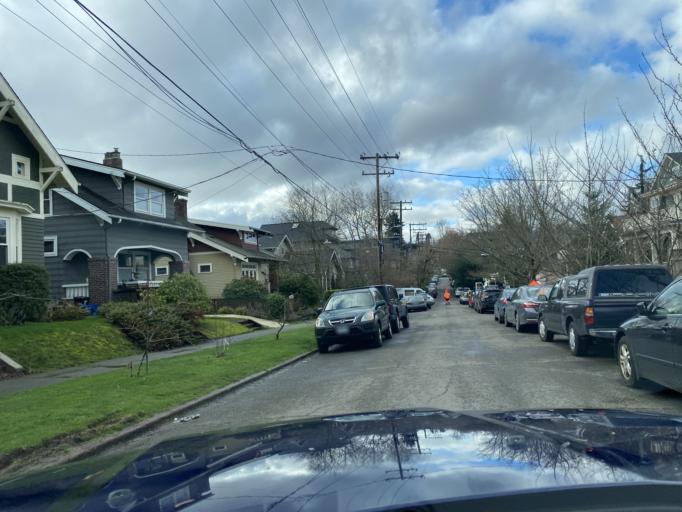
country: US
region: Washington
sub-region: King County
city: Seattle
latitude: 47.6244
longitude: -122.3048
